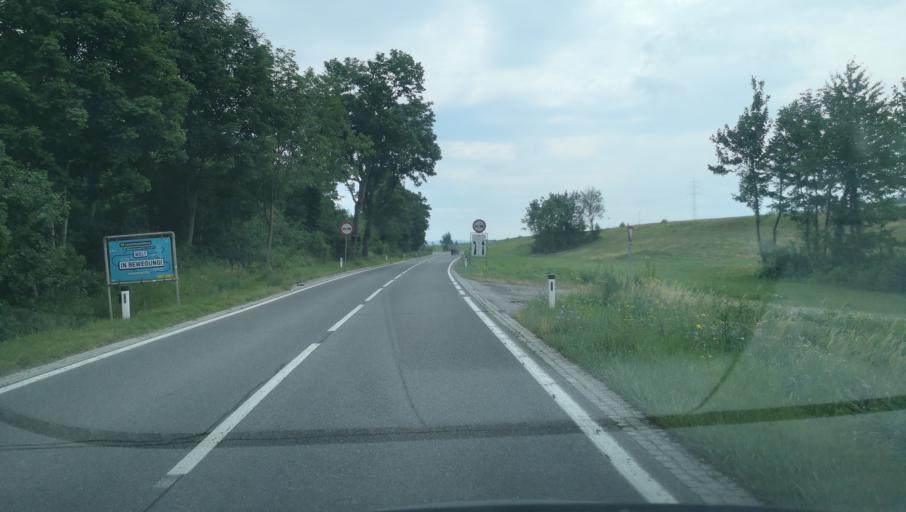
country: AT
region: Lower Austria
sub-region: Politischer Bezirk Melk
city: Klein-Poechlarn
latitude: 48.2228
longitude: 15.2447
